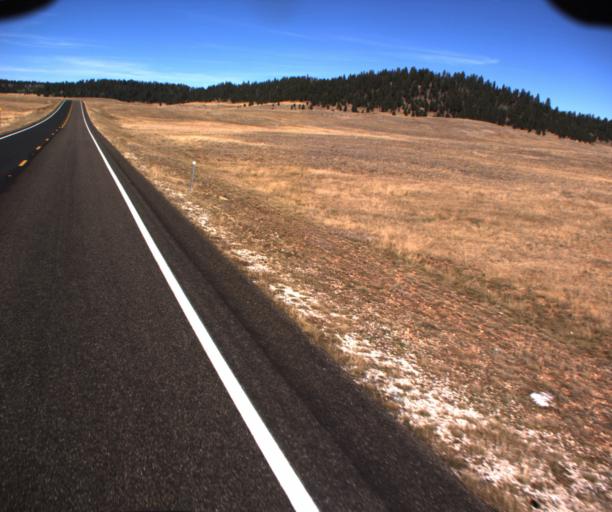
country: US
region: Arizona
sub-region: Coconino County
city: Grand Canyon
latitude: 36.4855
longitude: -112.1288
